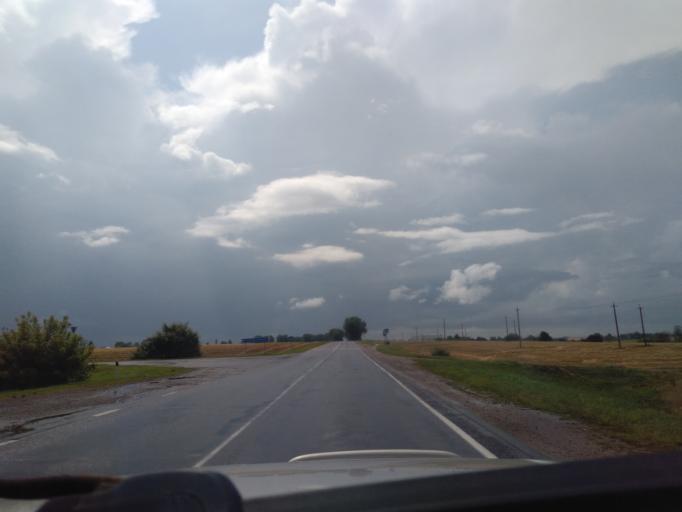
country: BY
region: Minsk
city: Tsimkavichy
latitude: 53.0977
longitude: 27.0418
